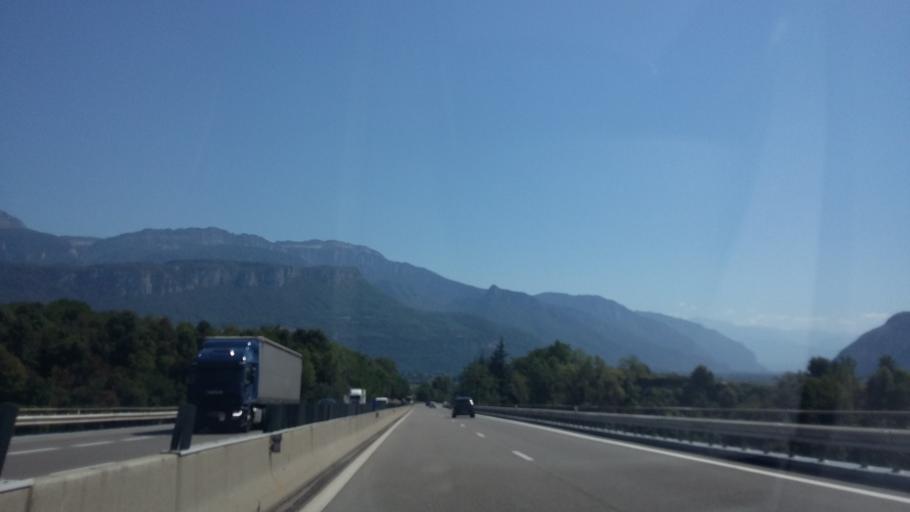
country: FR
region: Rhone-Alpes
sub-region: Departement de l'Isere
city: Saint-Jean-de-Moirans
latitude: 45.3431
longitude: 5.5692
